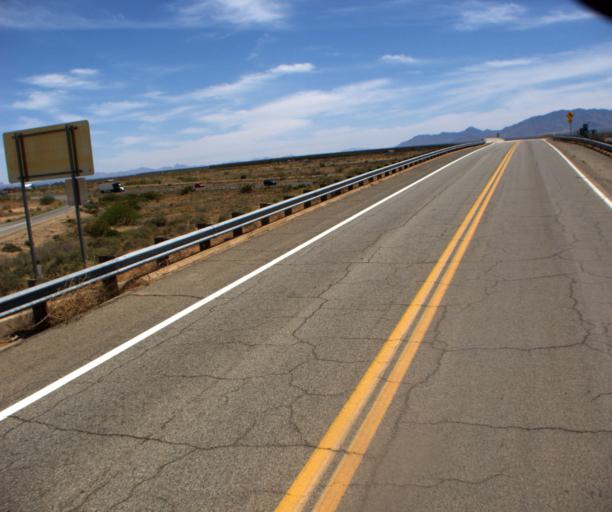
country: US
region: Arizona
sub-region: Cochise County
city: Willcox
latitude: 32.3185
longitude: -109.4506
